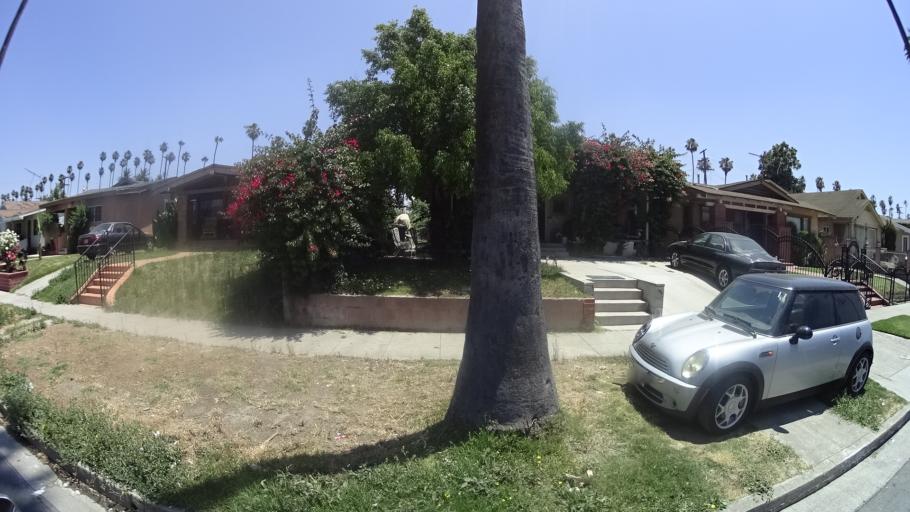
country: US
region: California
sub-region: Los Angeles County
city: View Park-Windsor Hills
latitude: 33.9957
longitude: -118.3171
